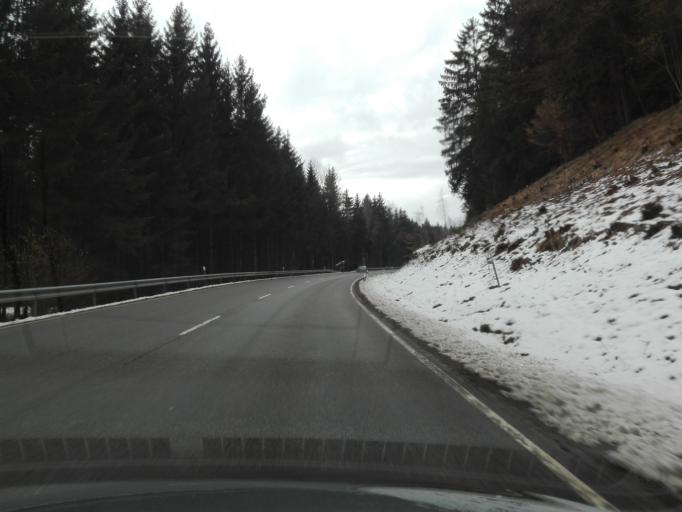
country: DE
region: Bavaria
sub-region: Lower Bavaria
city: Wegscheid
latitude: 48.5720
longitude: 13.7435
